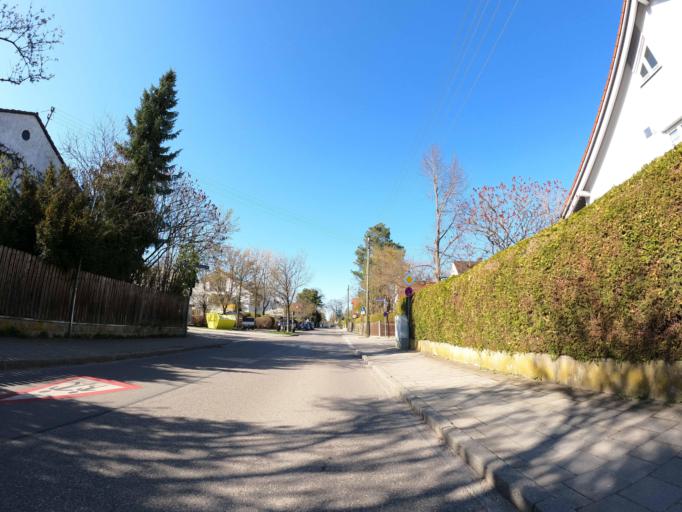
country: DE
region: Bavaria
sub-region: Upper Bavaria
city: Ottobrunn
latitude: 48.0732
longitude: 11.6770
